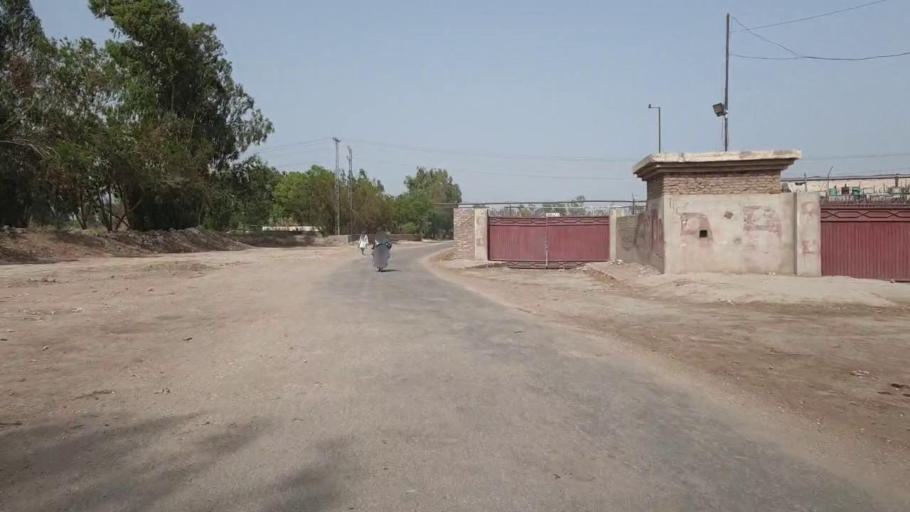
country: PK
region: Sindh
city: Daulatpur
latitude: 26.5588
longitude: 67.9849
